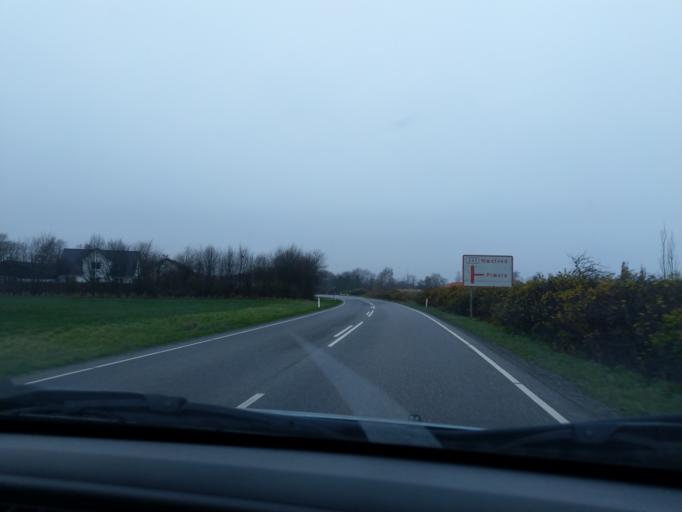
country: DK
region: Zealand
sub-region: Vordingborg Kommune
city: Praesto
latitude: 55.1118
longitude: 12.0630
